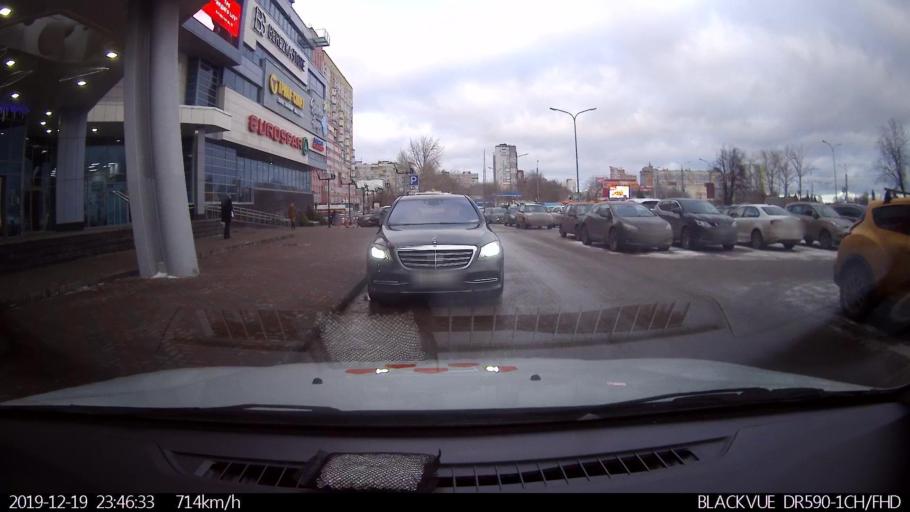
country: RU
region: Jaroslavl
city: Breytovo
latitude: 58.2166
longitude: 37.7361
